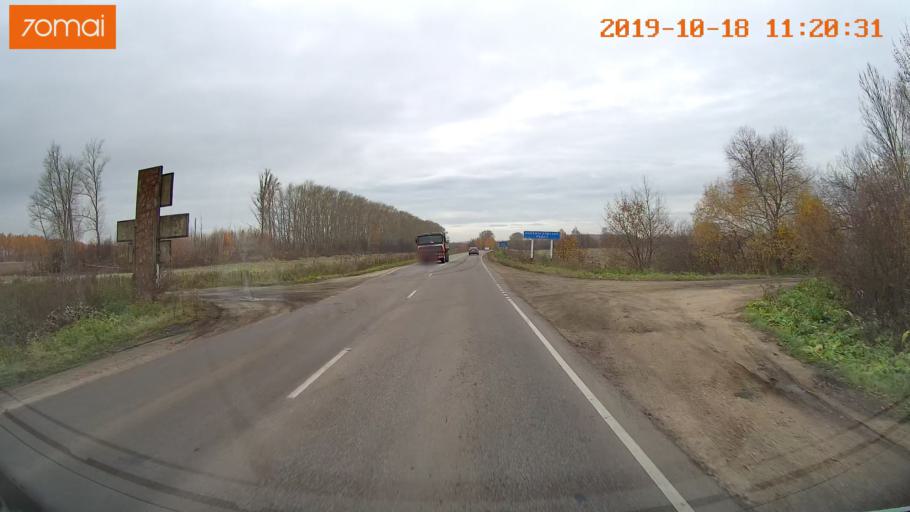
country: RU
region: Tula
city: Kimovsk
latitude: 54.0620
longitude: 38.5589
